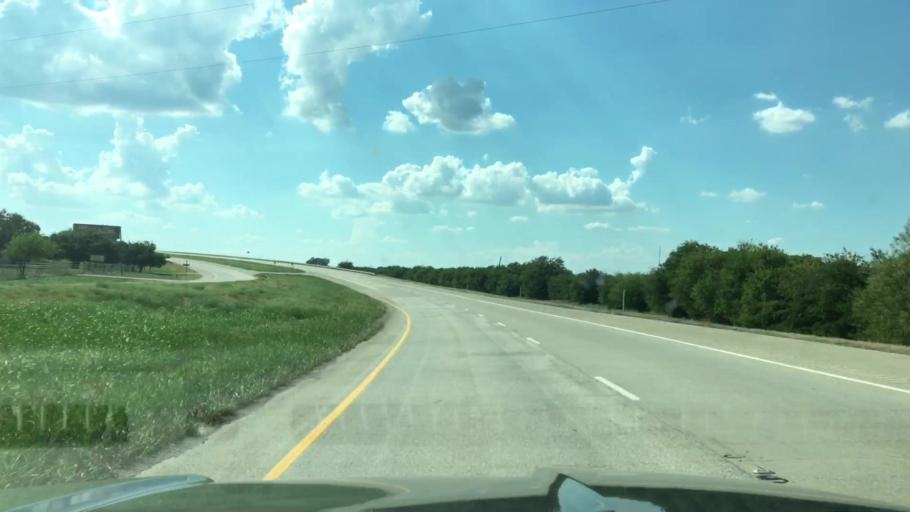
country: US
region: Texas
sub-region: Wise County
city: Rhome
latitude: 33.0457
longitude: -97.4547
